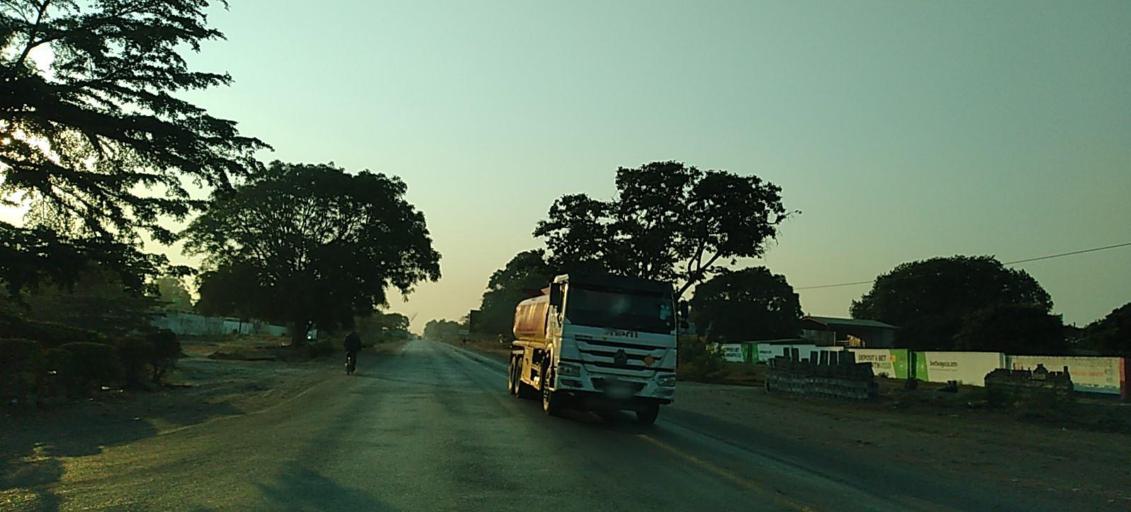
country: ZM
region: Copperbelt
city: Ndola
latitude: -13.0135
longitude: 28.6596
